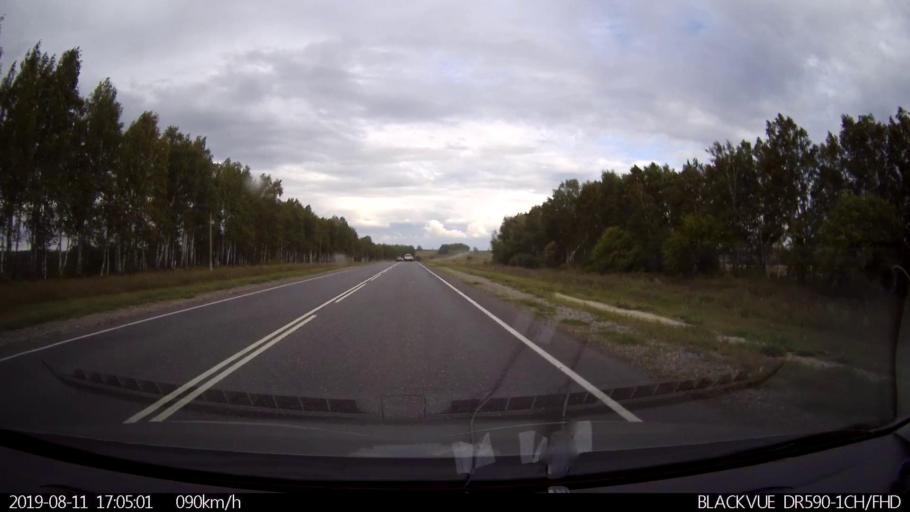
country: RU
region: Ulyanovsk
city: Mayna
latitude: 54.2995
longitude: 47.7771
